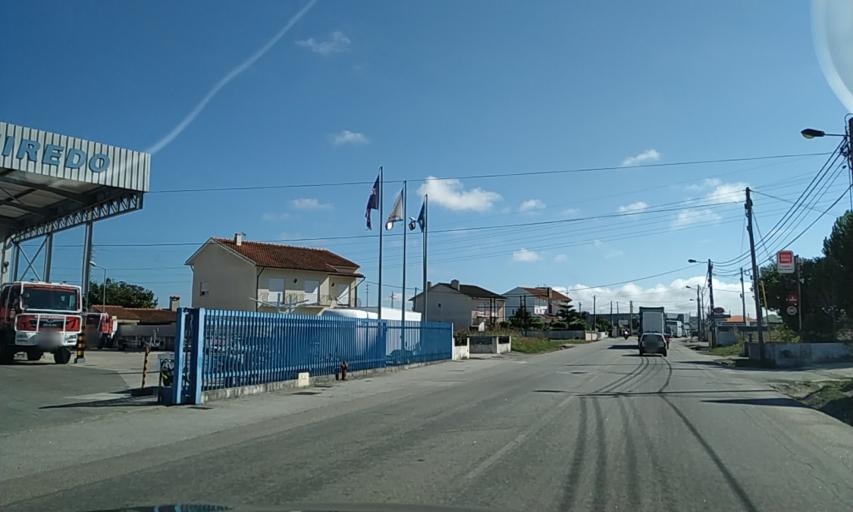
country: PT
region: Aveiro
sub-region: Aveiro
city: Aveiro
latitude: 40.6712
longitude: -8.6056
